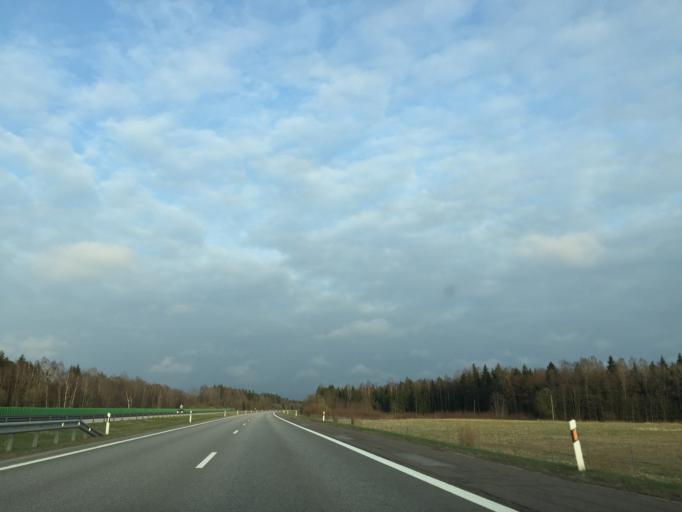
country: LT
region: Klaipedos apskritis
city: Gargzdai
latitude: 55.7055
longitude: 21.5894
